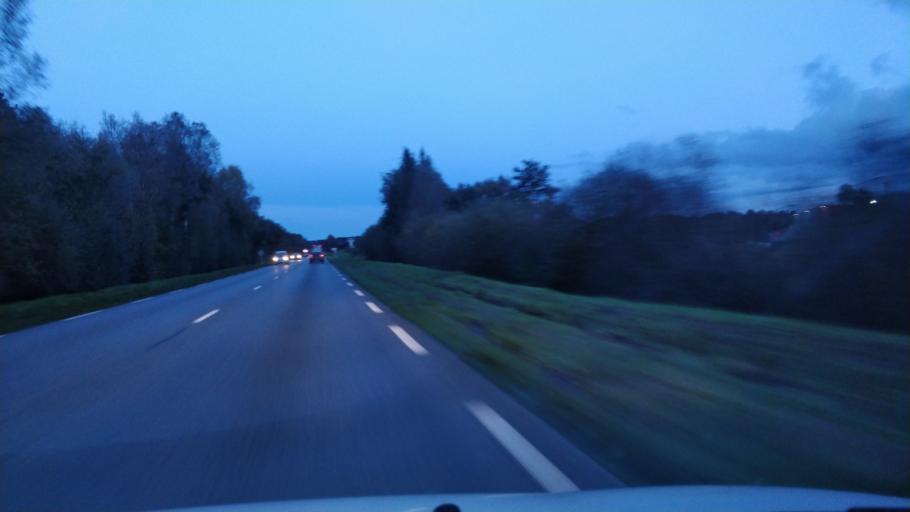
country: FR
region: Brittany
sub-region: Departement des Cotes-d'Armor
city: Plemet
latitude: 48.1707
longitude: -2.5867
